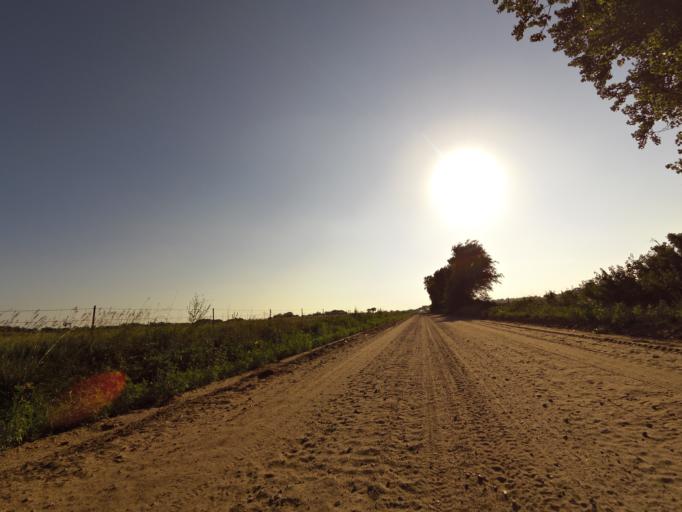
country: US
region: Kansas
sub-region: McPherson County
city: Inman
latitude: 38.1883
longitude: -97.8953
